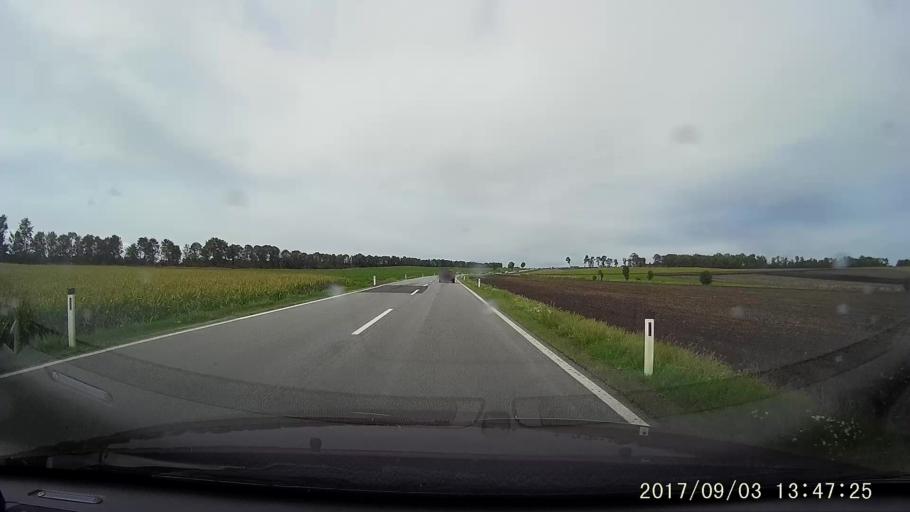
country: AT
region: Lower Austria
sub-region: Politischer Bezirk Hollabrunn
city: Guntersdorf
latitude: 48.6594
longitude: 16.0513
